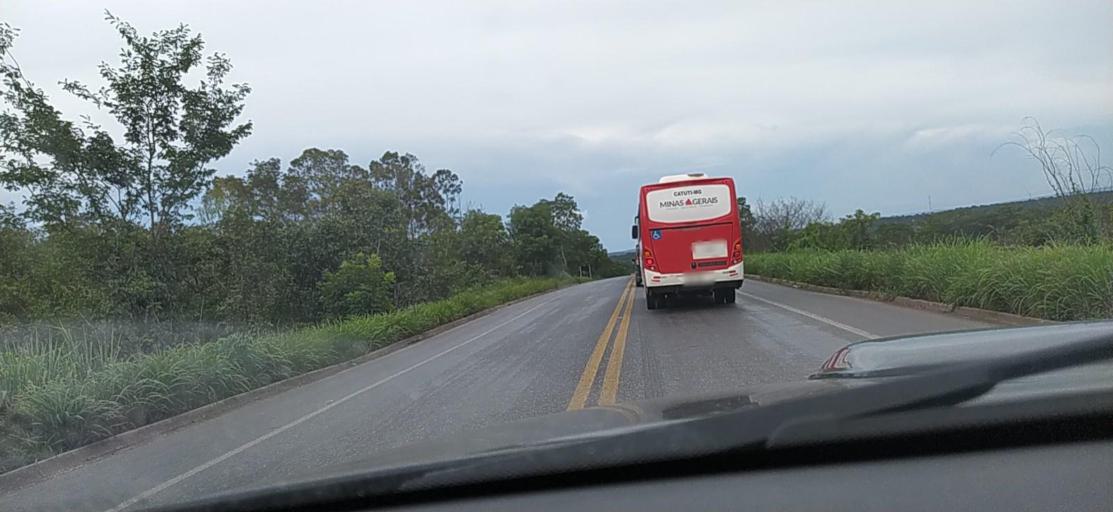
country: BR
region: Minas Gerais
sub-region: Montes Claros
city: Montes Claros
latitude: -16.6689
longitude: -43.7900
